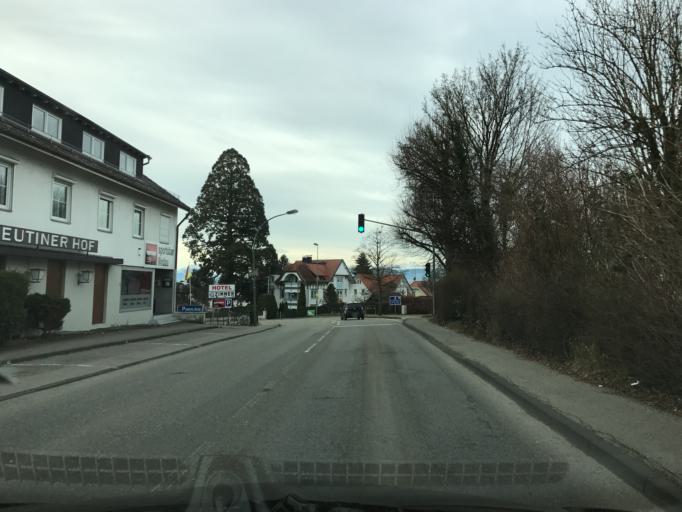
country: DE
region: Bavaria
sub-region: Swabia
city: Lindau
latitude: 47.5632
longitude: 9.7028
